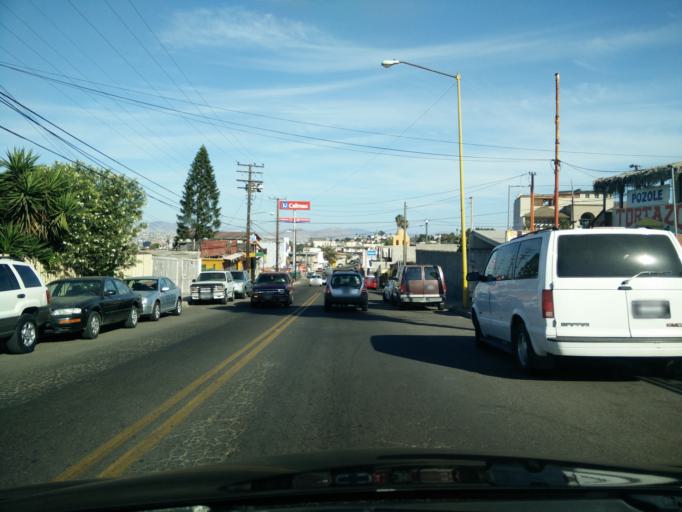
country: MX
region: Baja California
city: Tijuana
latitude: 32.5284
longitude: -117.0617
